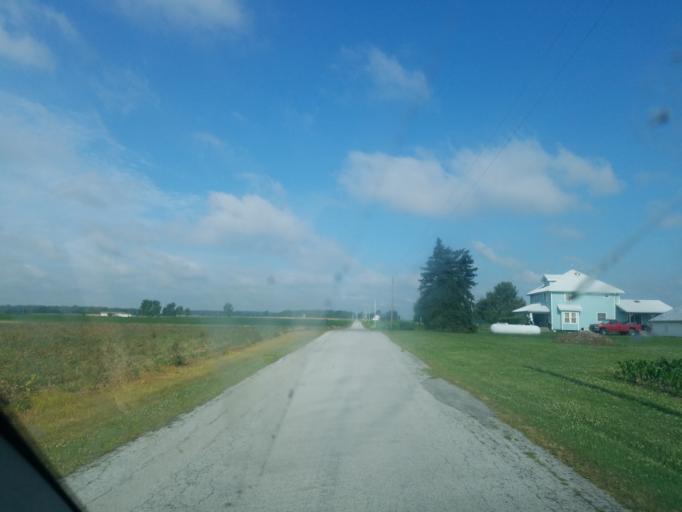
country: US
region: Ohio
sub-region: Hardin County
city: Kenton
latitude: 40.7179
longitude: -83.6845
